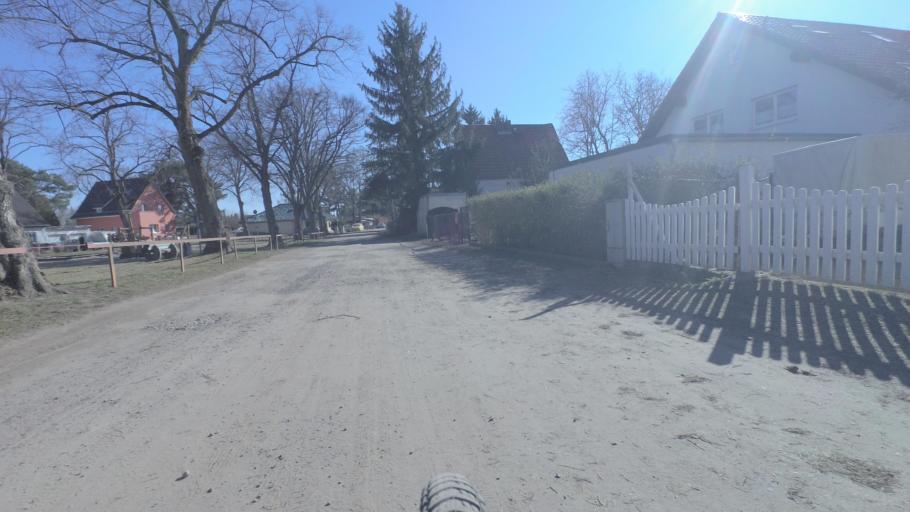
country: DE
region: Brandenburg
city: Rangsdorf
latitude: 52.2840
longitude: 13.4357
